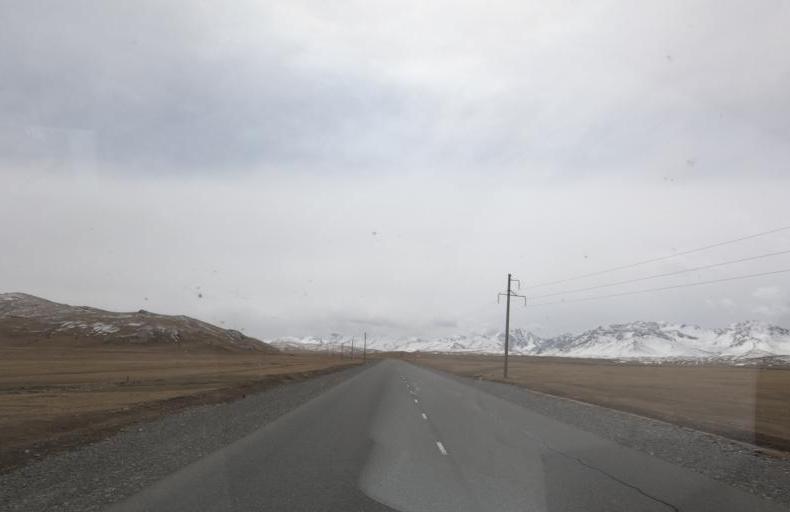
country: KG
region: Naryn
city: Baetov
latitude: 40.6105
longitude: 75.0517
